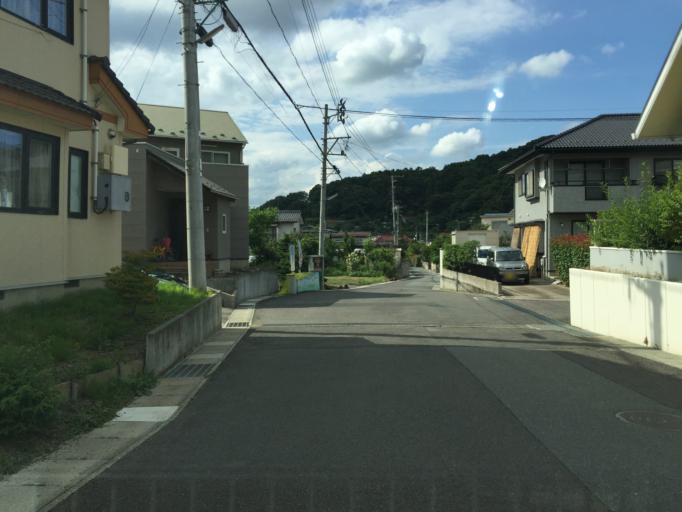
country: JP
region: Fukushima
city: Fukushima-shi
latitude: 37.7455
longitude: 140.4890
